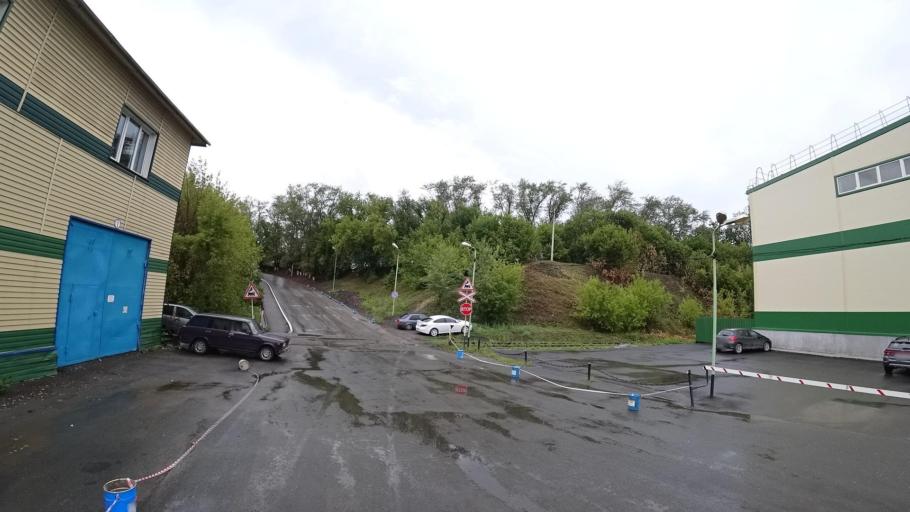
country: RU
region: Sverdlovsk
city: Kamyshlov
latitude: 56.8503
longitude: 62.7090
